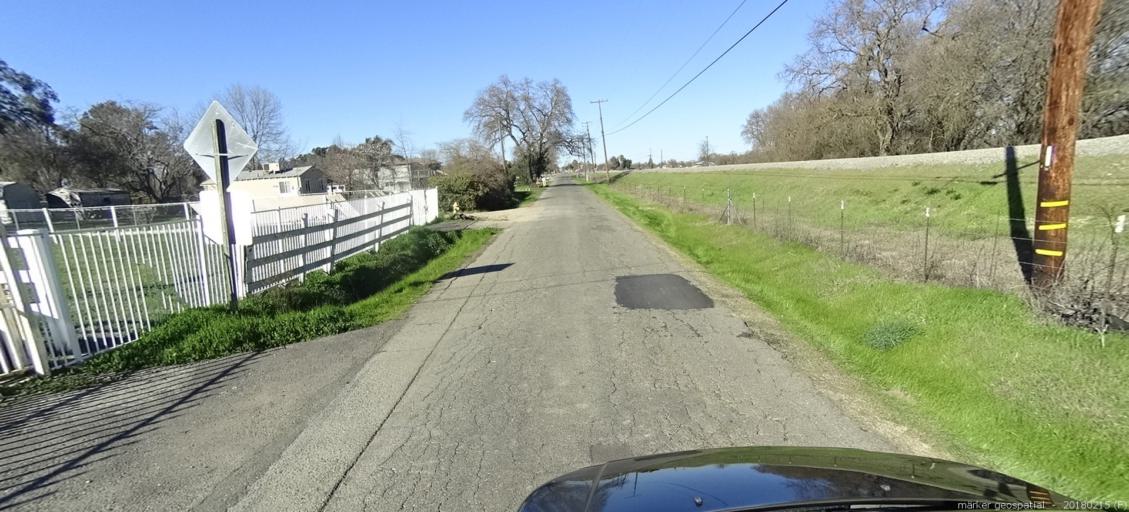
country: US
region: California
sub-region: Sacramento County
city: Rio Linda
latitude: 38.6711
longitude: -121.4569
